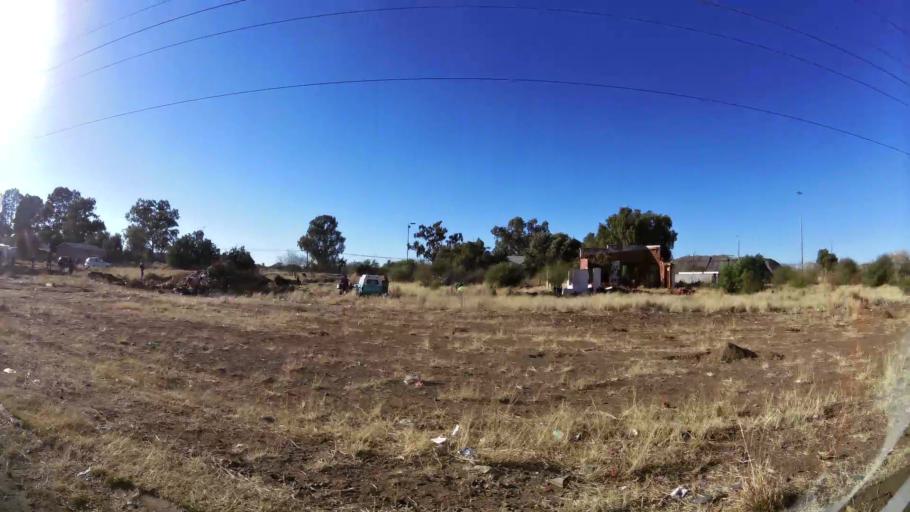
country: ZA
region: Northern Cape
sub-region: Frances Baard District Municipality
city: Kimberley
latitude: -28.7614
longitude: 24.7830
